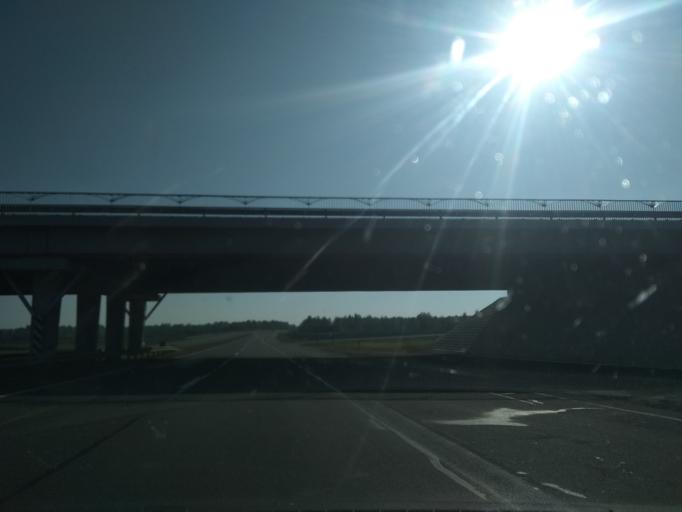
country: BY
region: Brest
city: Horad Kobryn
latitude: 52.2188
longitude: 24.4227
